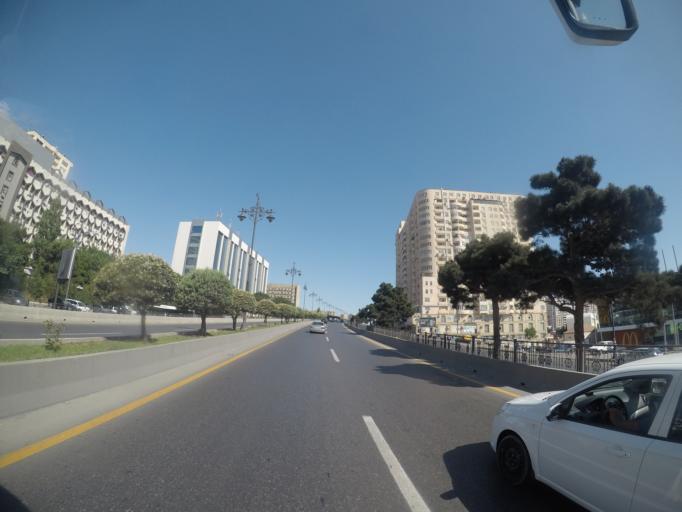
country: AZ
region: Baki
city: Khodzhi-Gasan
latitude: 40.4011
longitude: 49.8099
